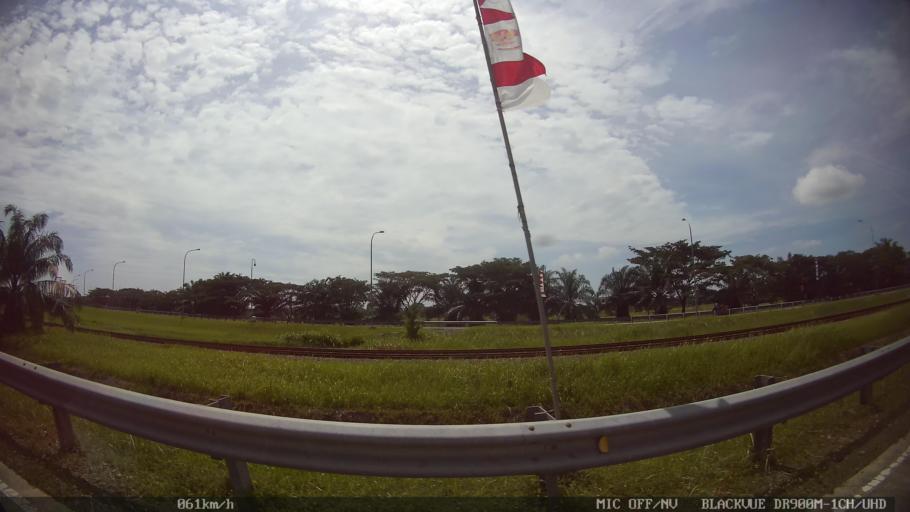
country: ID
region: North Sumatra
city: Percut
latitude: 3.6288
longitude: 98.8721
